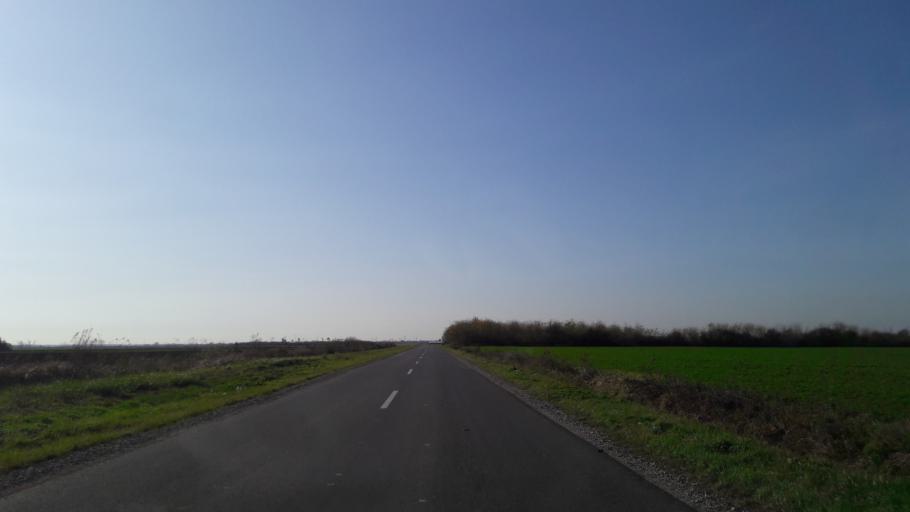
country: HR
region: Osjecko-Baranjska
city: Antunovac
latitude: 45.4799
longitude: 18.7115
